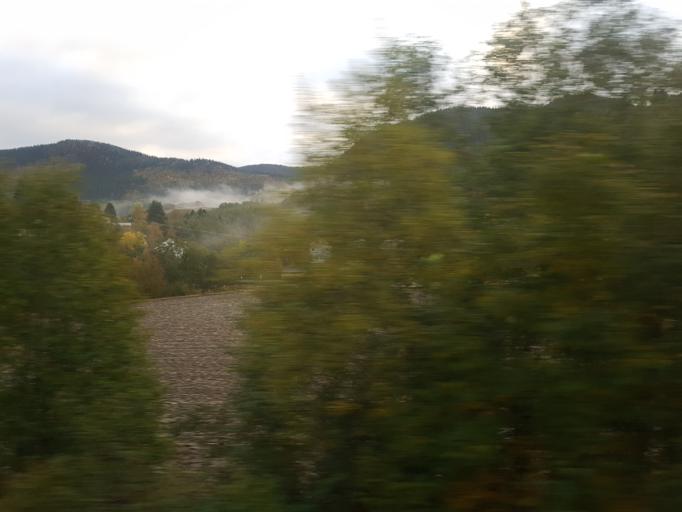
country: NO
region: Sor-Trondelag
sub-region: Melhus
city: Melhus
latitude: 63.3117
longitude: 10.2941
